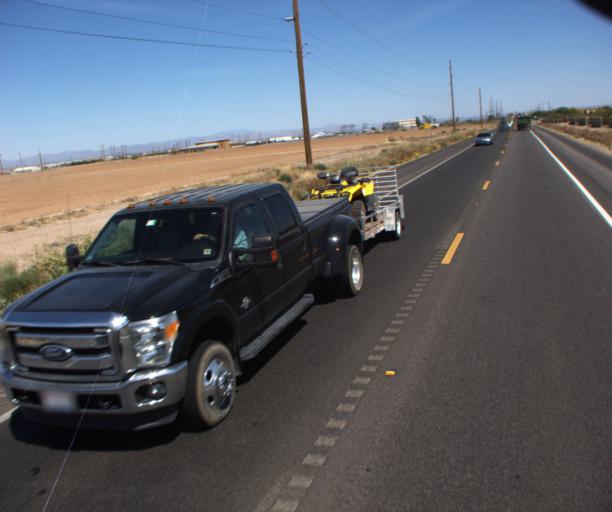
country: US
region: Arizona
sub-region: Pinal County
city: Coolidge
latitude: 33.0025
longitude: -111.5298
